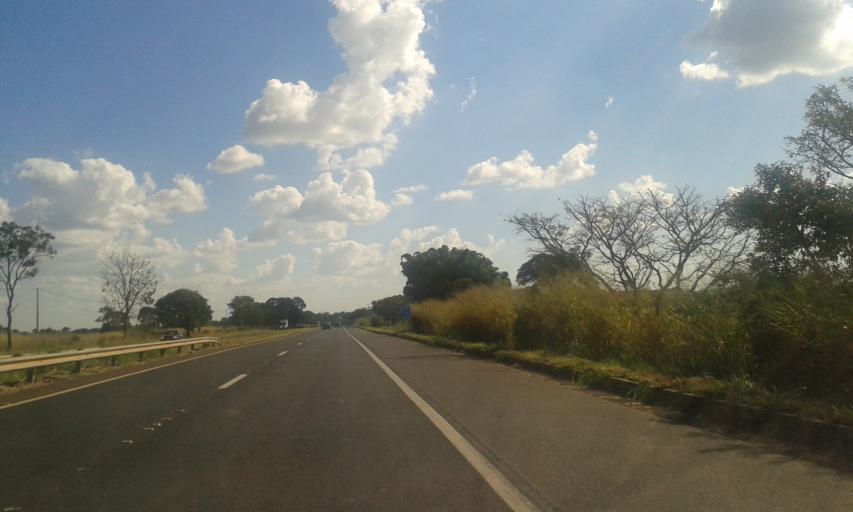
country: BR
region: Minas Gerais
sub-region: Monte Alegre De Minas
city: Monte Alegre de Minas
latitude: -18.8924
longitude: -48.6432
